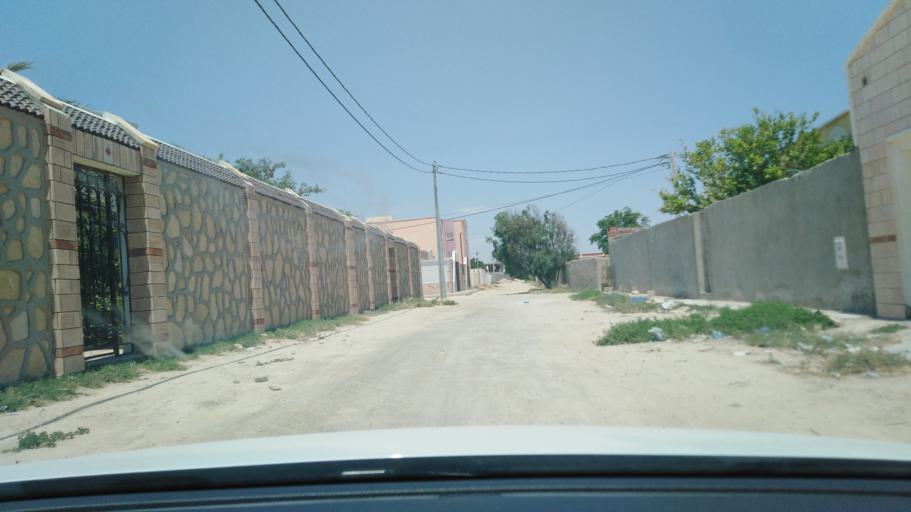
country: TN
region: Qabis
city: Gabes
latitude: 33.9469
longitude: 10.0720
